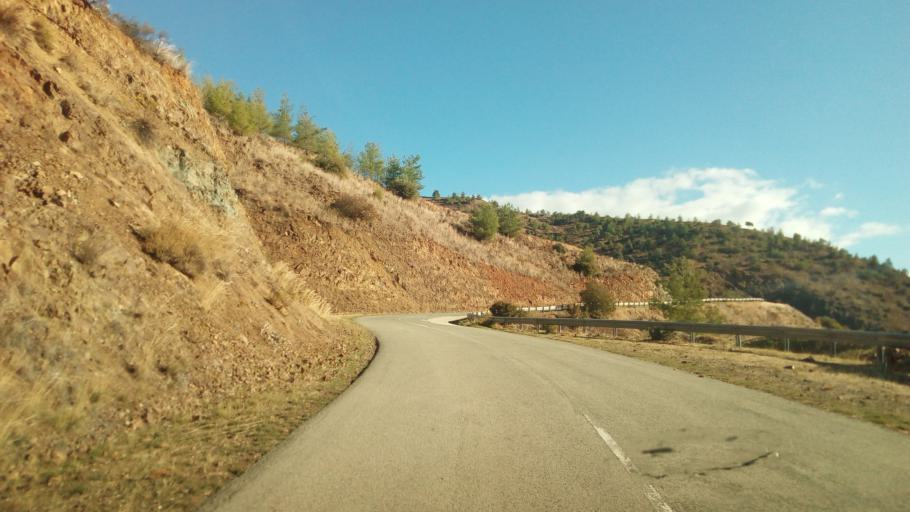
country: CY
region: Lefkosia
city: Lefka
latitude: 35.0755
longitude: 32.8043
